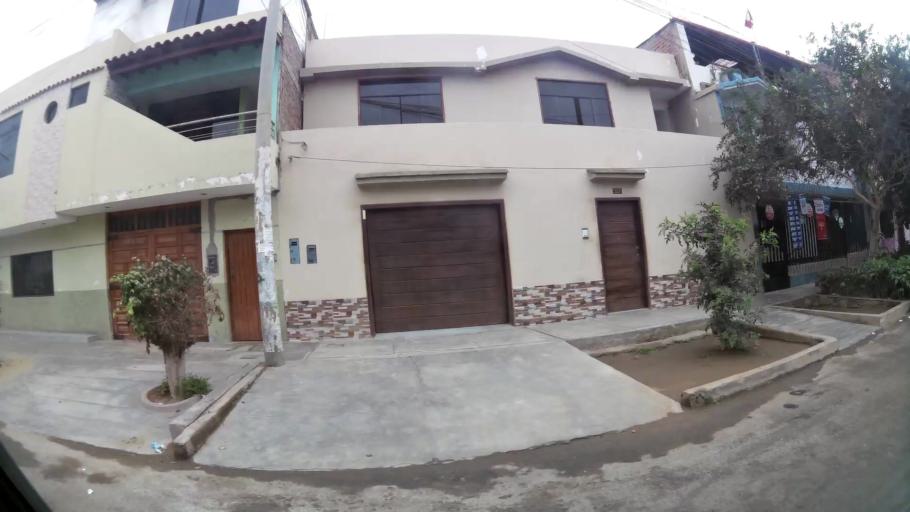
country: PE
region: La Libertad
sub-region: Provincia de Trujillo
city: Buenos Aires
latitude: -8.1373
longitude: -79.0479
